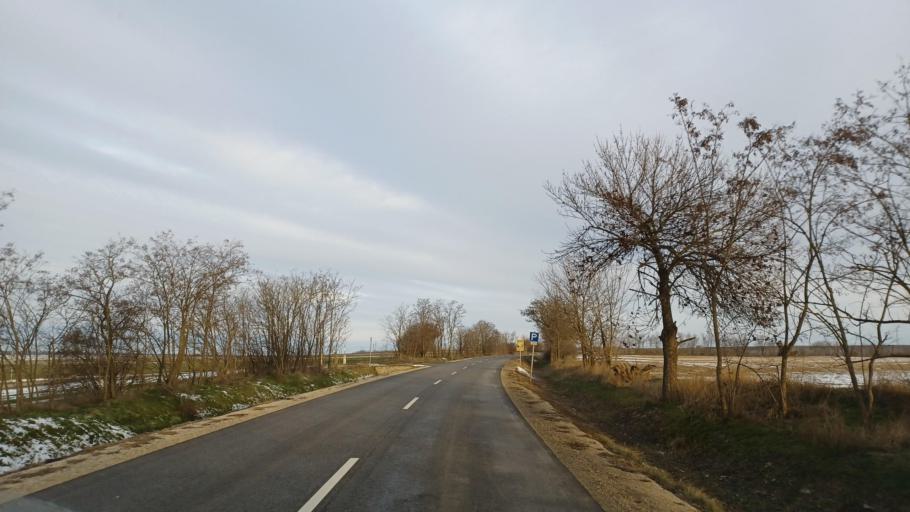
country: HU
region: Tolna
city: Paks
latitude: 46.6359
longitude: 18.8495
